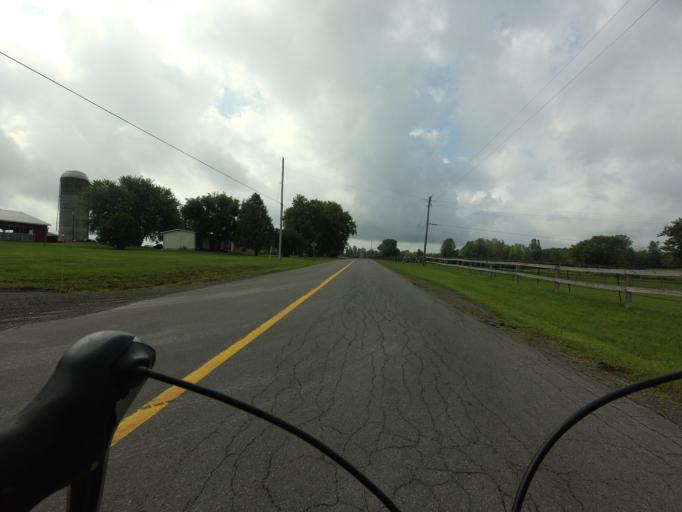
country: CA
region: Ontario
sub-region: Lanark County
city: Smiths Falls
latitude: 44.9697
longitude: -75.8089
